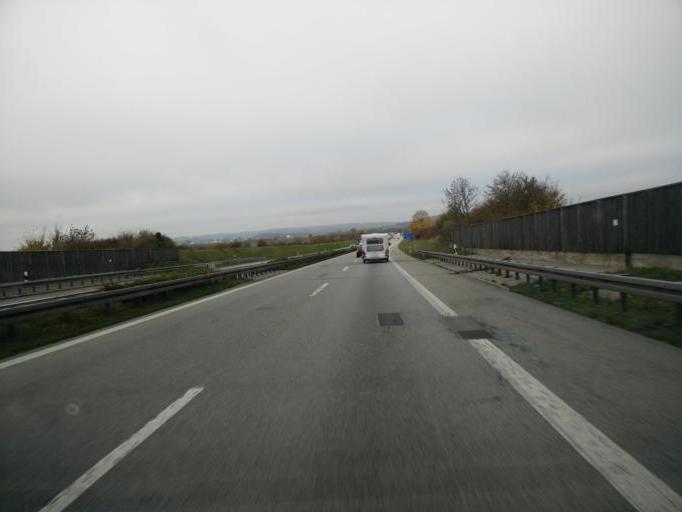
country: DE
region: Bavaria
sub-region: Swabia
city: Apfeltrach
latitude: 48.0318
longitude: 10.5313
